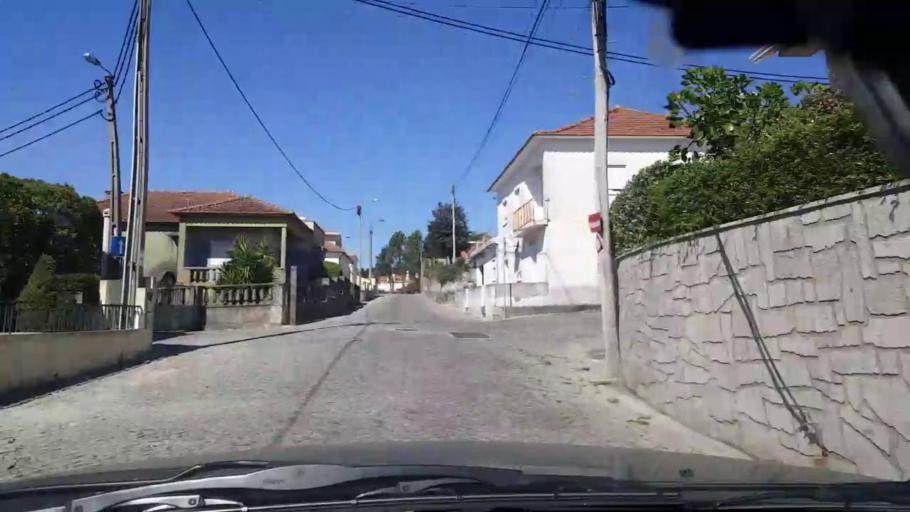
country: PT
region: Porto
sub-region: Vila do Conde
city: Arvore
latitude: 41.3177
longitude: -8.6739
